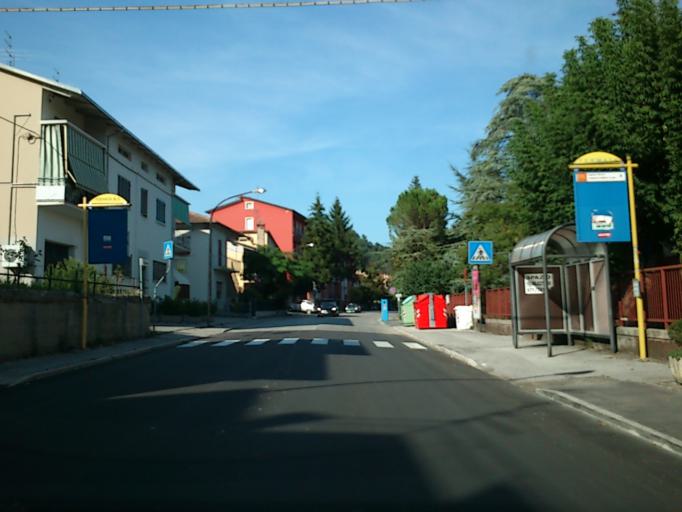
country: IT
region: The Marches
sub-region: Provincia di Pesaro e Urbino
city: Fermignano
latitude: 43.6923
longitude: 12.6447
